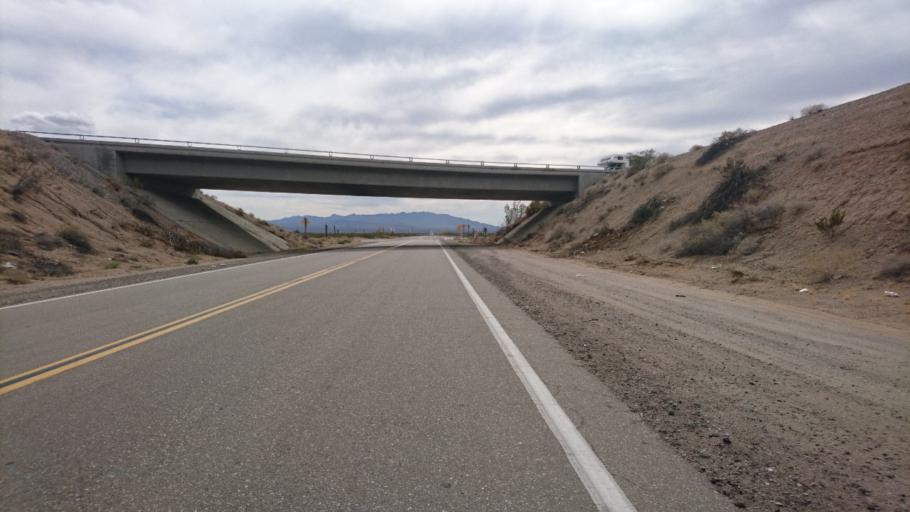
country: US
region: California
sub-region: San Bernardino County
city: Needles
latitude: 34.8123
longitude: -115.1902
